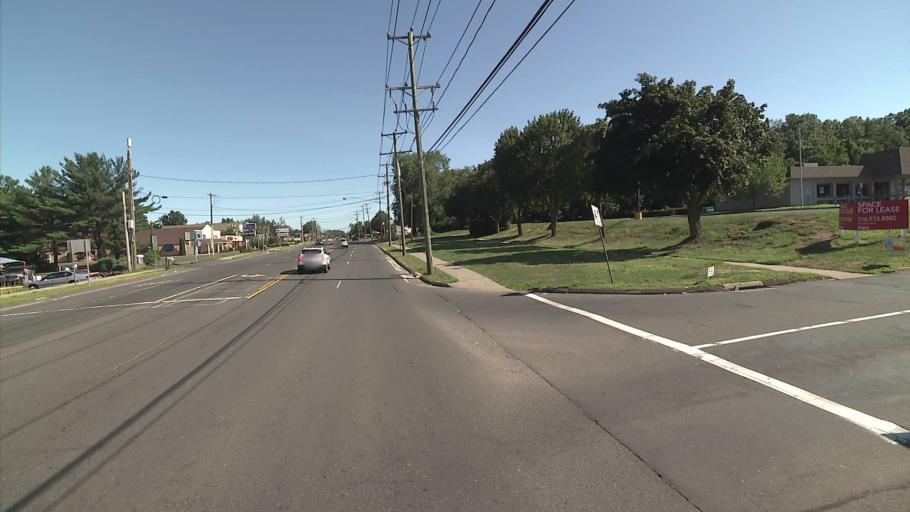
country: US
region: Connecticut
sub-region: Hartford County
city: Plainville
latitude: 41.6230
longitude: -72.8730
